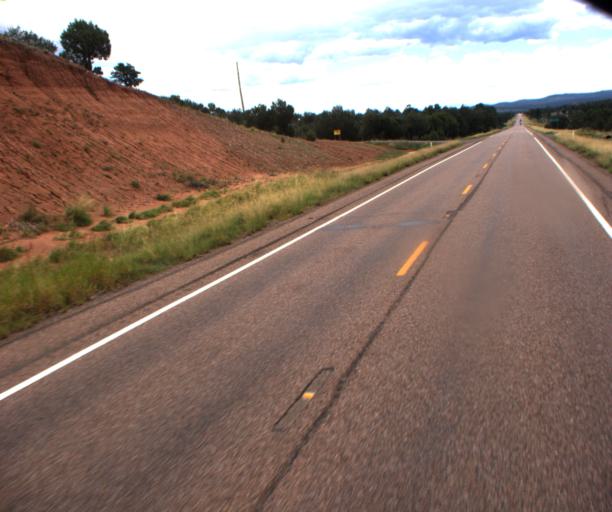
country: US
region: Arizona
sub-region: Navajo County
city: Linden
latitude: 34.3343
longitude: -110.2701
